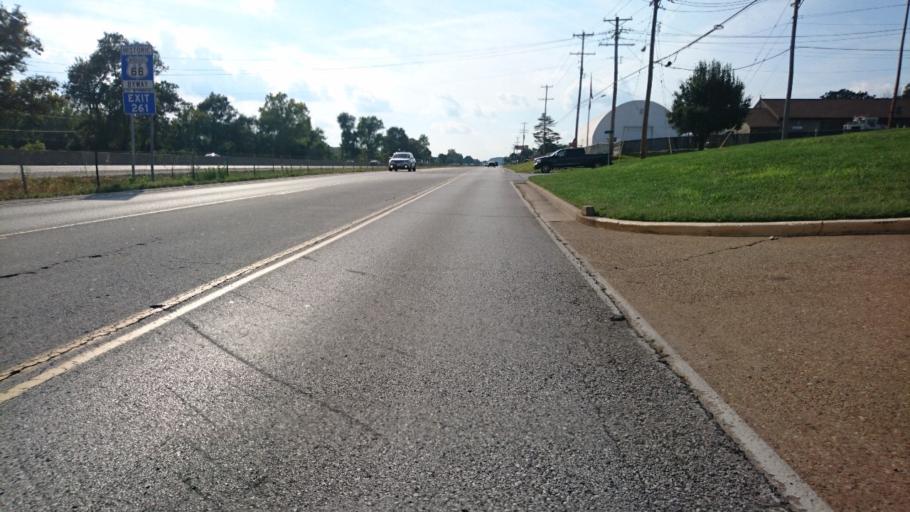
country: US
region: Missouri
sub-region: Saint Louis County
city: Eureka
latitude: 38.5042
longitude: -90.6439
